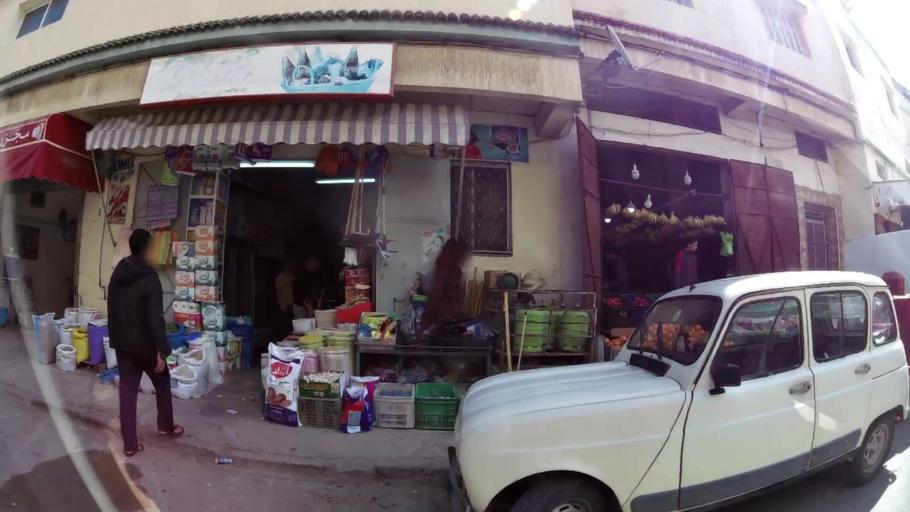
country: MA
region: Tanger-Tetouan
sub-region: Tanger-Assilah
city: Tangier
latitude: 35.7703
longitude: -5.7688
